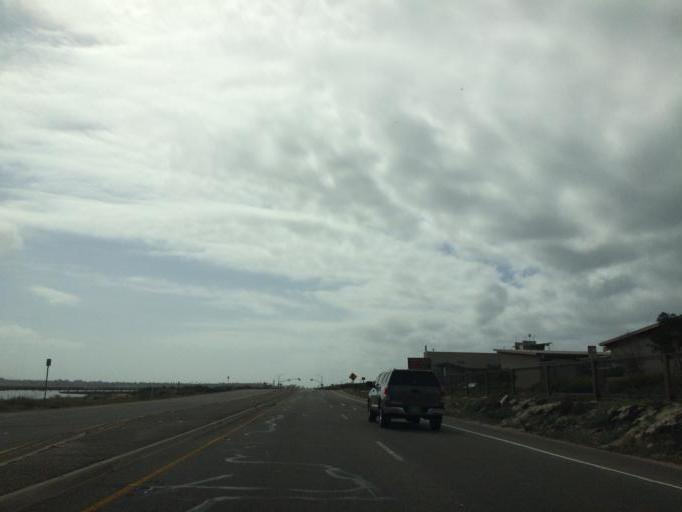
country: US
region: California
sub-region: Orange County
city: Huntington Beach
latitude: 33.6980
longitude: -118.0494
